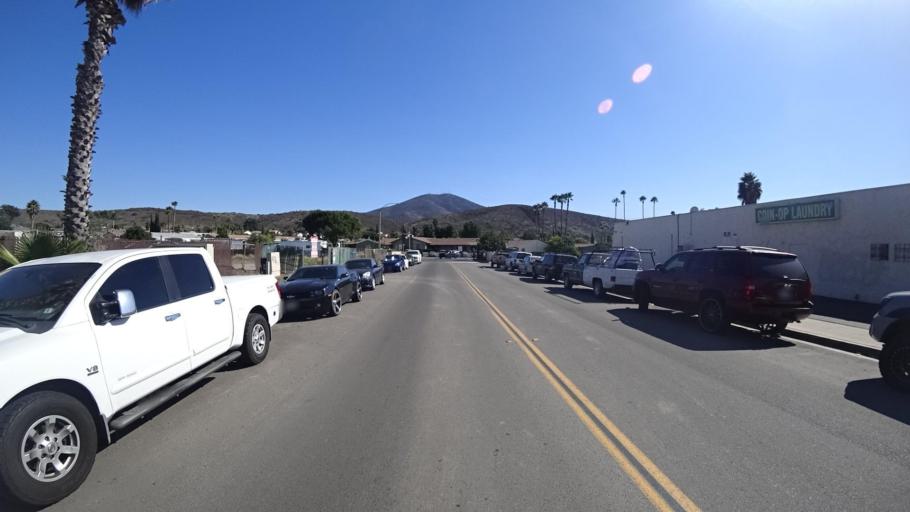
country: US
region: California
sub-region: San Diego County
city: Rancho San Diego
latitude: 32.7293
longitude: -116.9616
